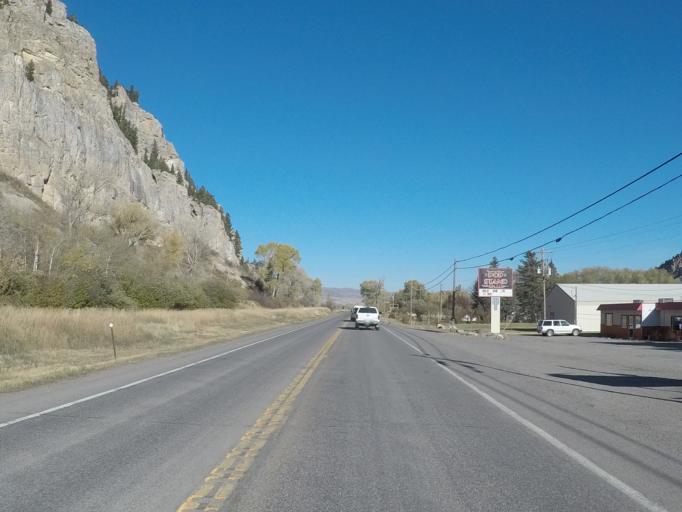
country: US
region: Montana
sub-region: Park County
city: Livingston
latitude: 45.6084
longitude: -110.5761
